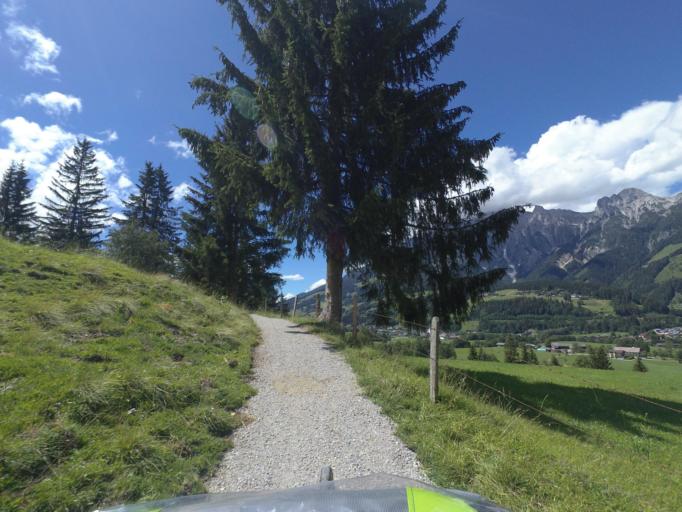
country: AT
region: Salzburg
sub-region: Politischer Bezirk Zell am See
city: Leogang
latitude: 47.4321
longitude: 12.7706
